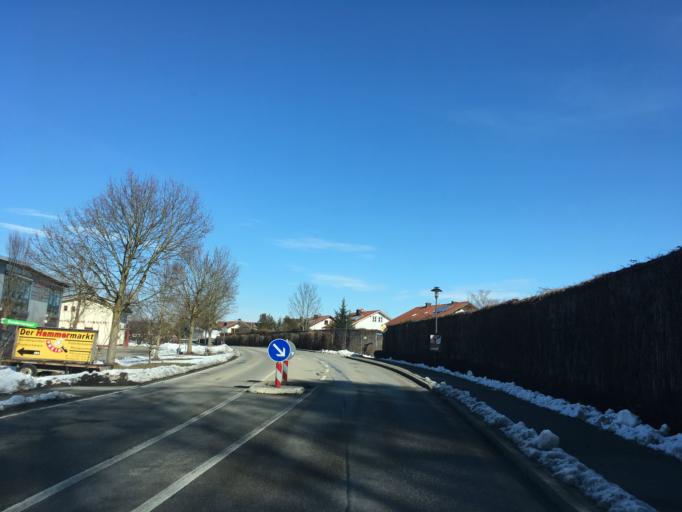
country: DE
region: Bavaria
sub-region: Upper Bavaria
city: Edling
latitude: 48.0641
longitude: 12.1576
